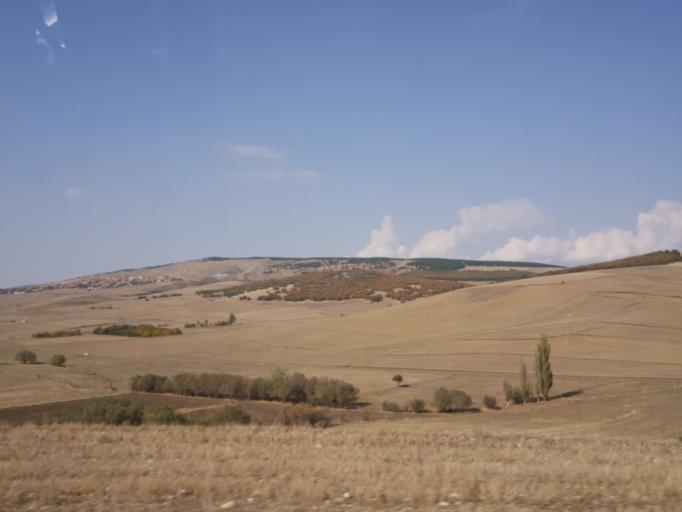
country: TR
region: Corum
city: Bogazkale
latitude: 40.1675
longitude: 34.6657
